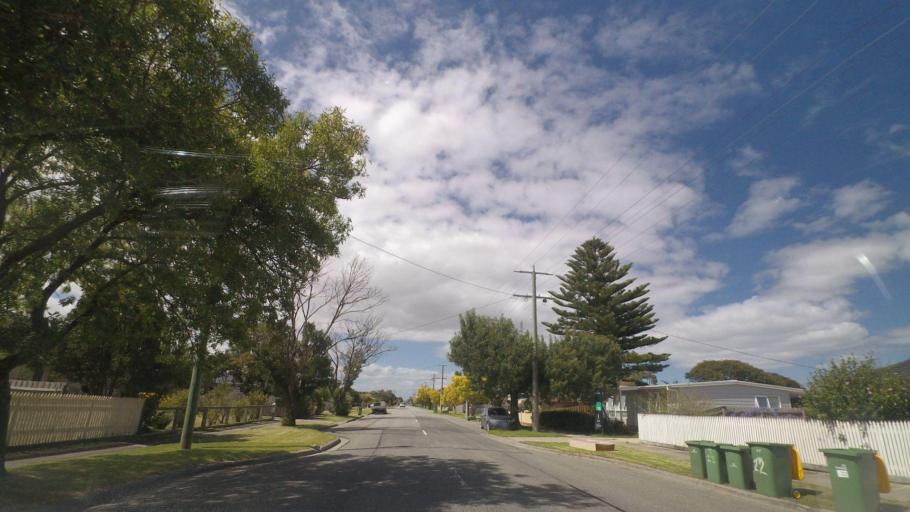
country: AU
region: Victoria
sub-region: Cardinia
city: Koo-Wee-Rup
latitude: -38.2022
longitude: 145.4891
